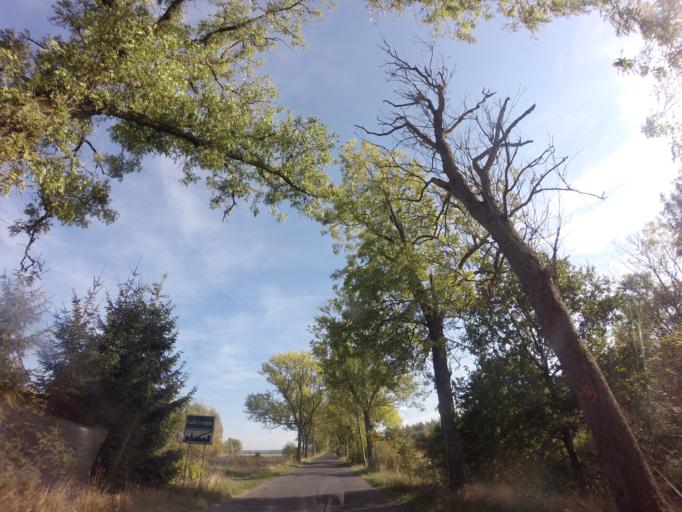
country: PL
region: West Pomeranian Voivodeship
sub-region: Powiat choszczenski
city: Recz
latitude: 53.2151
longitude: 15.6143
